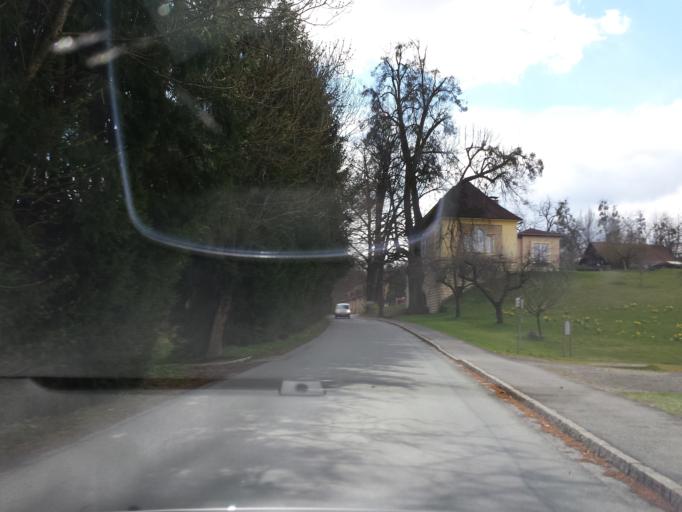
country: AT
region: Styria
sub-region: Politischer Bezirk Deutschlandsberg
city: Deutschlandsberg
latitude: 46.8149
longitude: 15.2430
